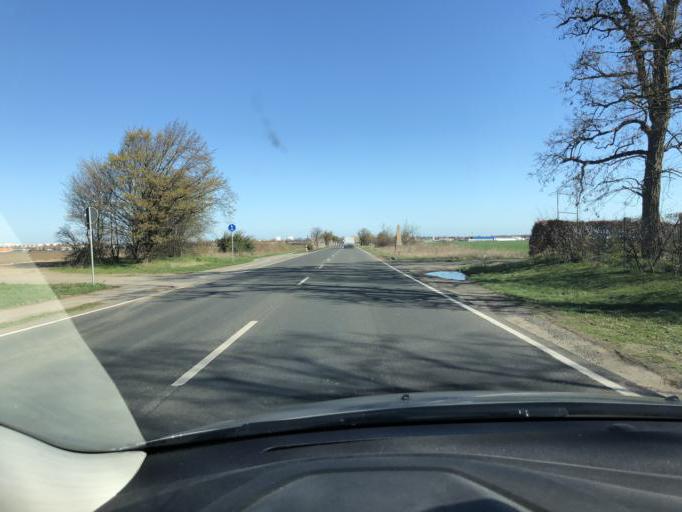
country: DE
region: Saxony-Anhalt
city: Magdeburg
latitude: 52.0689
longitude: 11.6158
